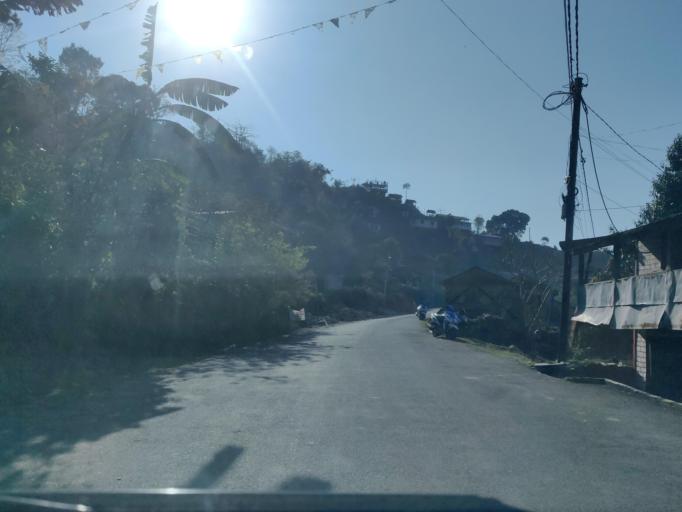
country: NP
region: Western Region
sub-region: Gandaki Zone
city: Pokhara
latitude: 28.2364
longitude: 83.9657
